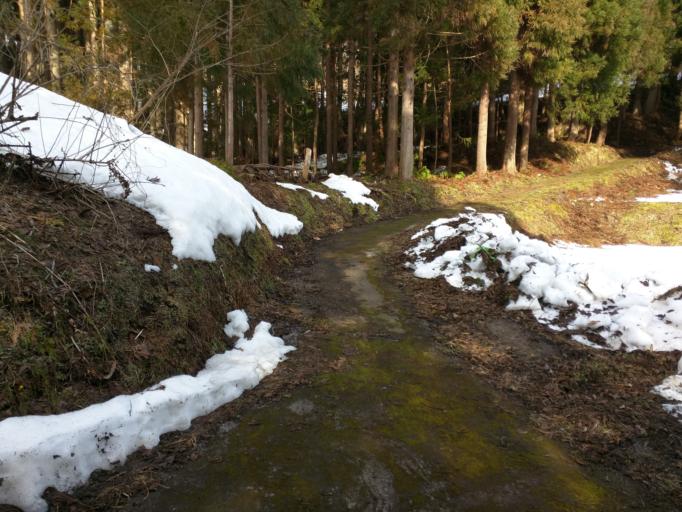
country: JP
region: Fukushima
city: Kitakata
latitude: 37.7078
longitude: 139.8053
